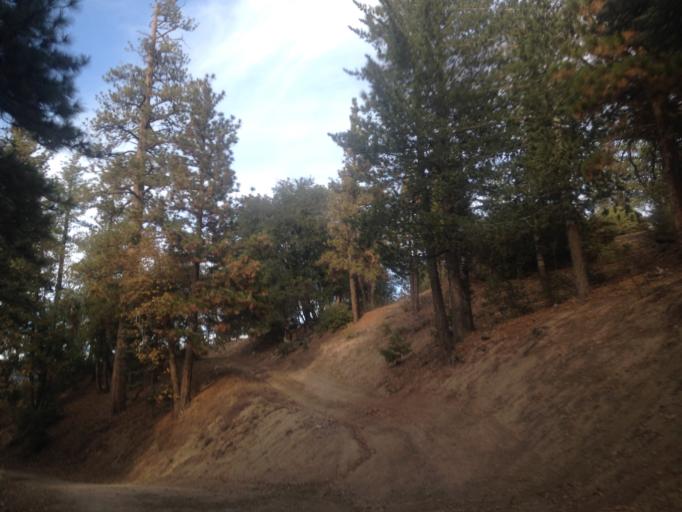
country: US
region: California
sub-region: San Bernardino County
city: Big Bear Lake
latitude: 34.1494
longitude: -116.9890
